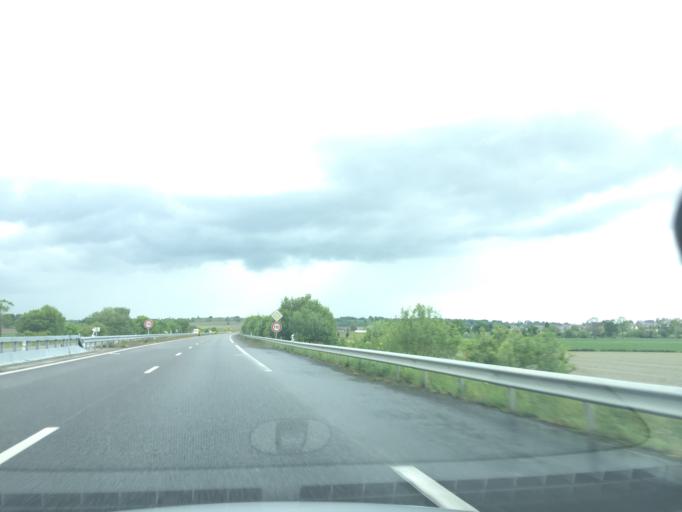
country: FR
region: Lower Normandy
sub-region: Departement de la Manche
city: Pontorson
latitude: 48.5618
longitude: -1.5386
